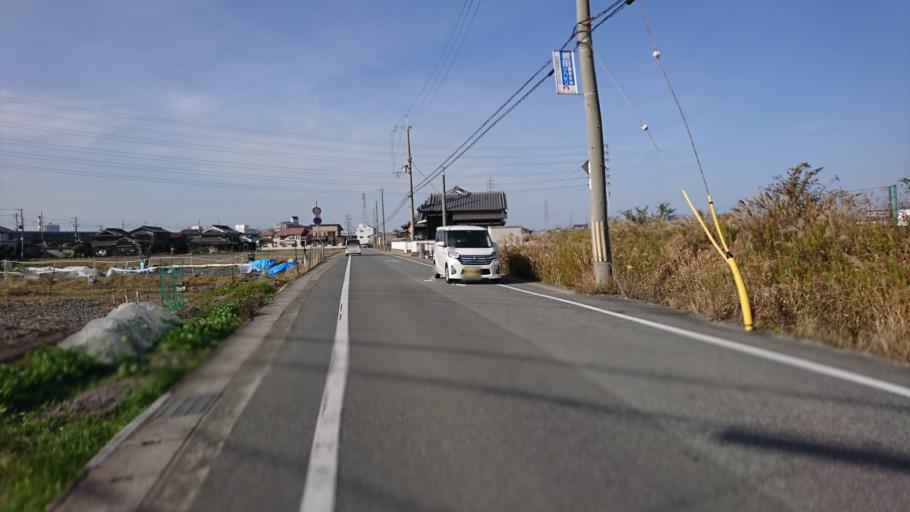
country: JP
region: Hyogo
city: Kakogawacho-honmachi
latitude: 34.7291
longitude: 134.8569
